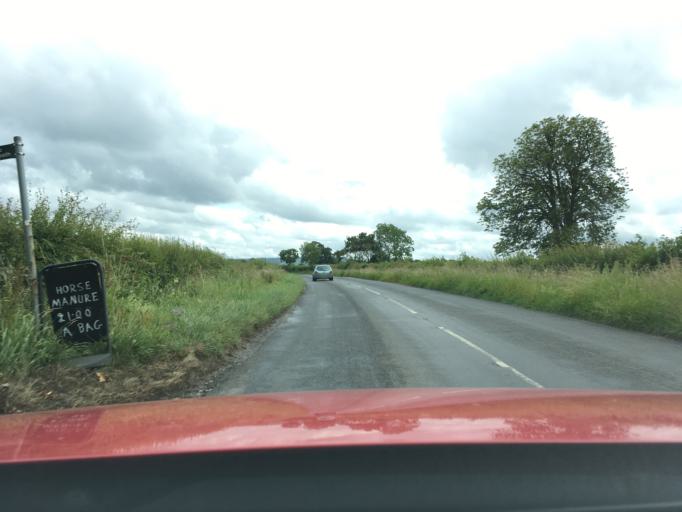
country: GB
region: England
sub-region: Worcestershire
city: Evesham
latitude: 52.0262
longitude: -1.9611
